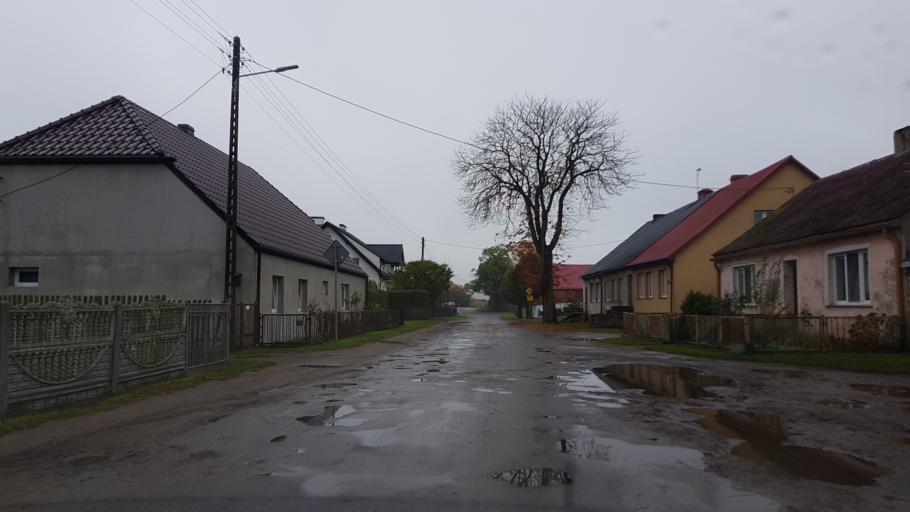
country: PL
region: West Pomeranian Voivodeship
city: Trzcinsko Zdroj
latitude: 53.0589
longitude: 14.5351
